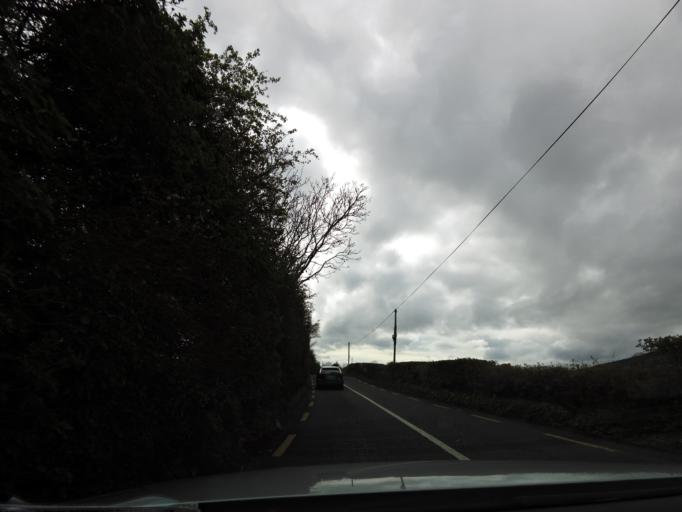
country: IE
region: Leinster
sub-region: Kilkenny
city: Ballyragget
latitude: 52.7250
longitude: -7.4768
